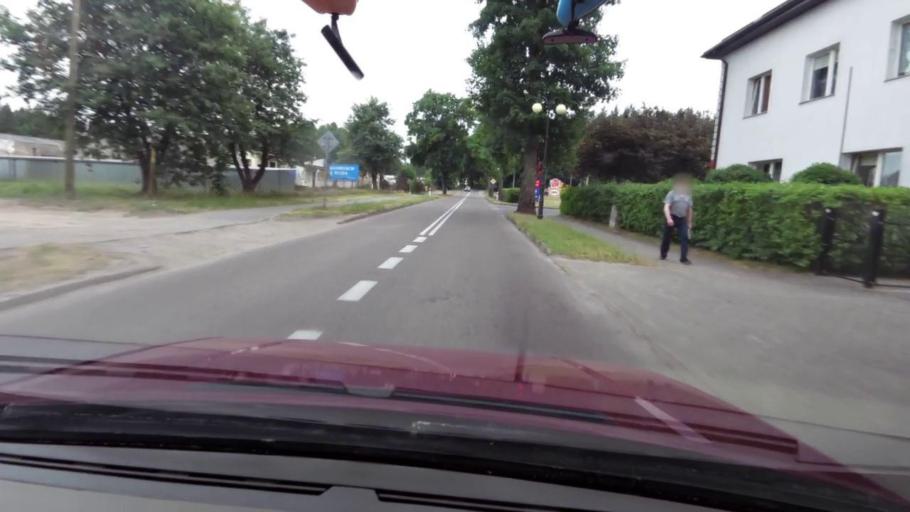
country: PL
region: Pomeranian Voivodeship
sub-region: Powiat slupski
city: Kepice
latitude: 54.2369
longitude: 16.8903
